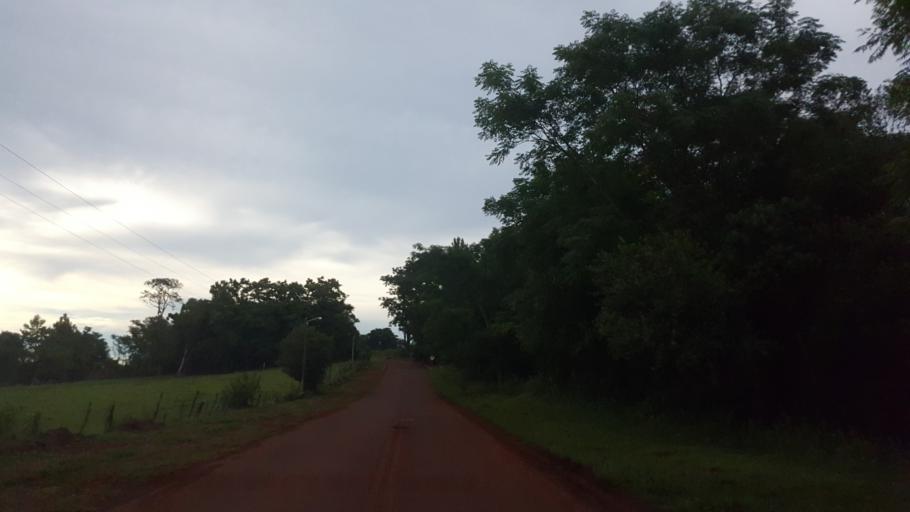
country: AR
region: Misiones
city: Santo Pipo
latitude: -27.1135
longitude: -55.3726
